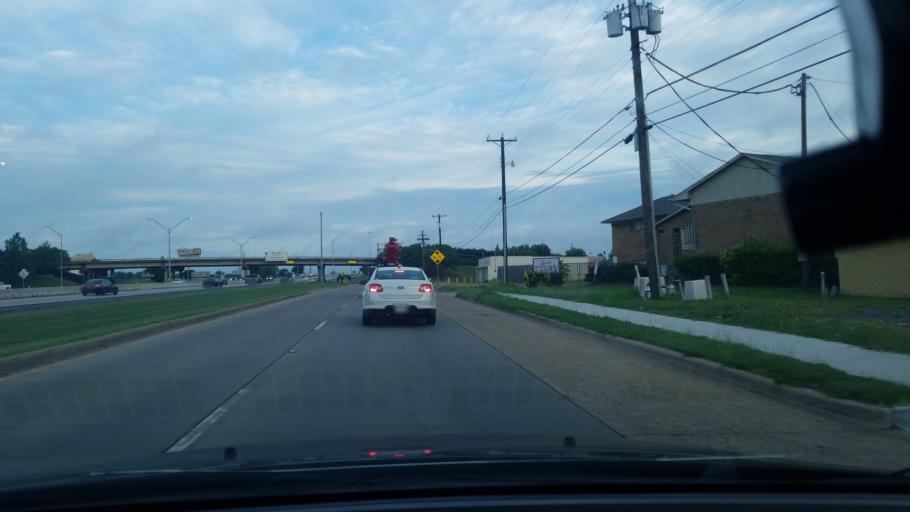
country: US
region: Texas
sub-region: Dallas County
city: Mesquite
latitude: 32.7970
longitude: -96.6661
